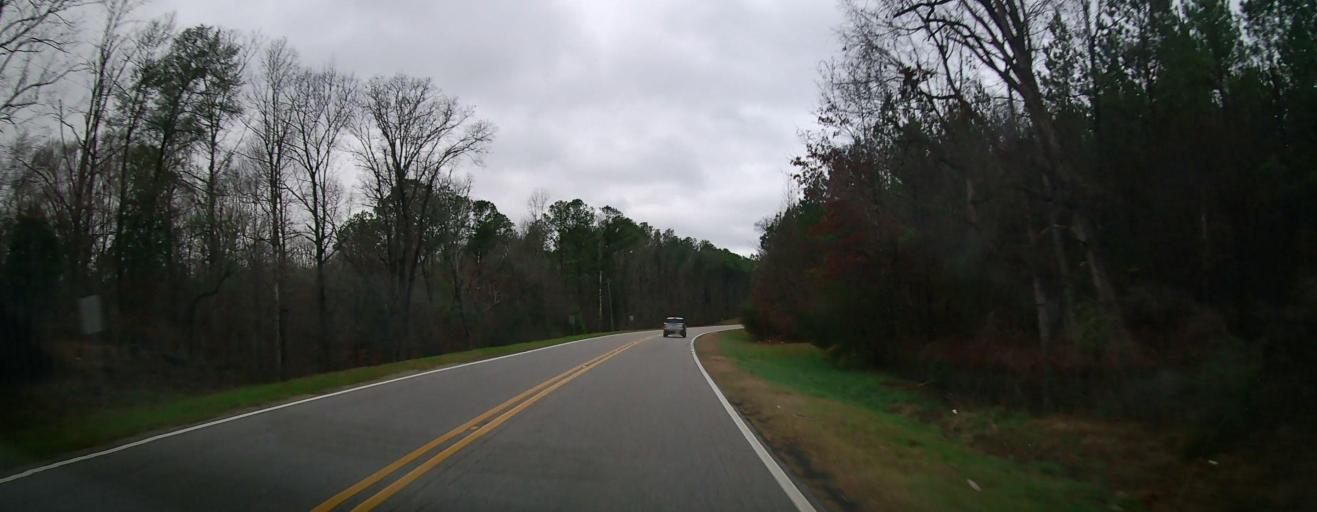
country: US
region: Alabama
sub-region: Bibb County
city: Centreville
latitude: 32.9064
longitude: -87.0156
